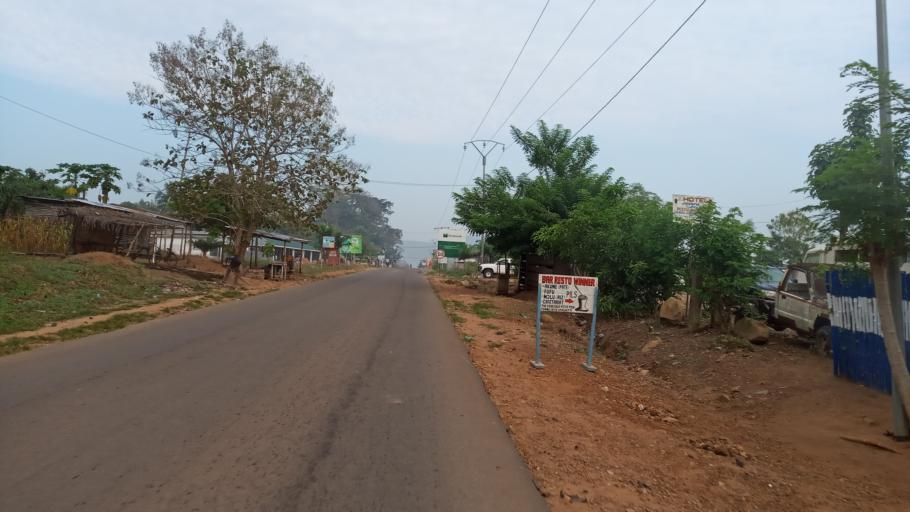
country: TG
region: Plateaux
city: Kpalime
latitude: 6.8898
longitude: 0.6422
